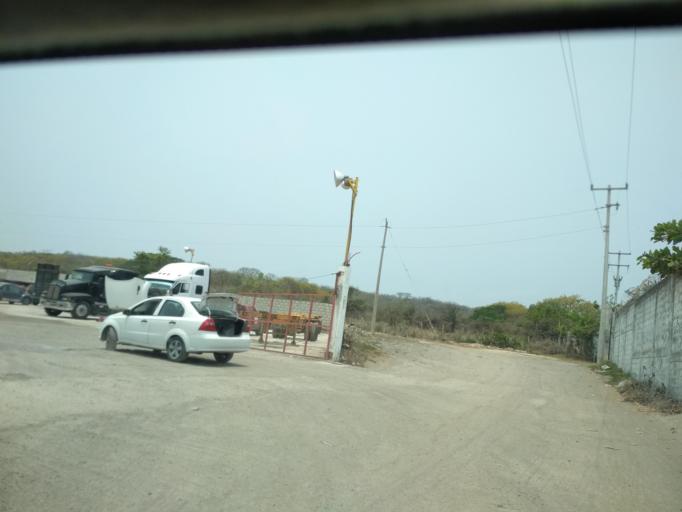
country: MX
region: Veracruz
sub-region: Veracruz
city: Delfino Victoria (Santa Fe)
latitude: 19.2257
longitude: -96.2607
